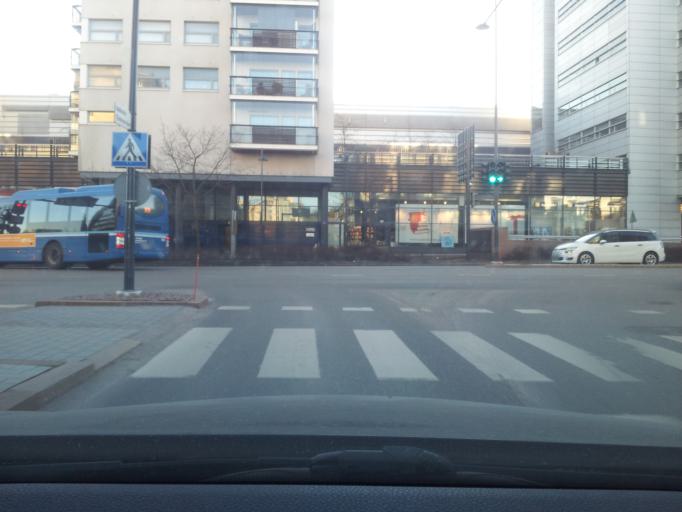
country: FI
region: Uusimaa
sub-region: Helsinki
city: Koukkuniemi
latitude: 60.1618
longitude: 24.7402
